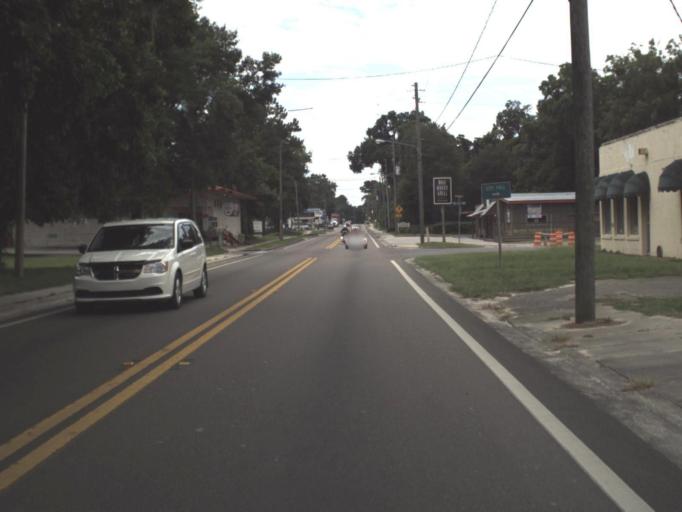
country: US
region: Florida
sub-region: Alachua County
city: Archer
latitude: 29.5334
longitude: -82.5191
